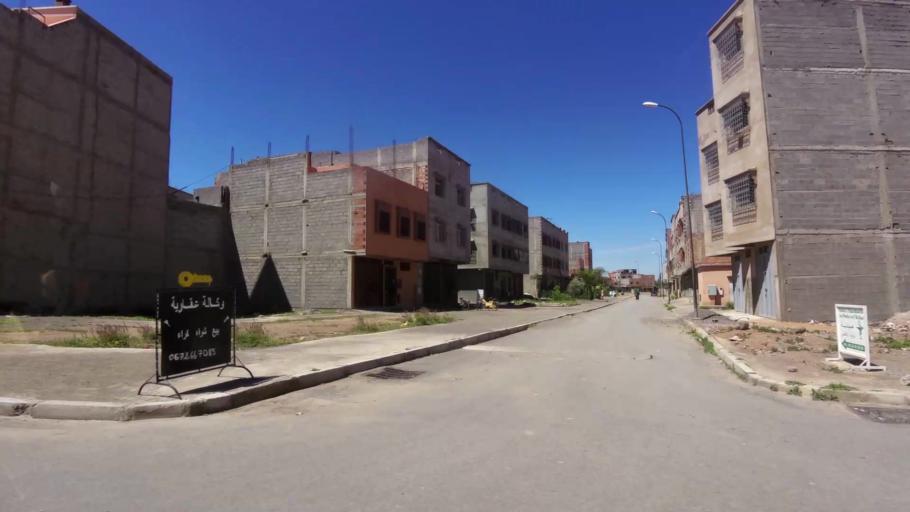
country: MA
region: Marrakech-Tensift-Al Haouz
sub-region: Marrakech
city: Marrakesh
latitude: 31.5535
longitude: -7.9790
